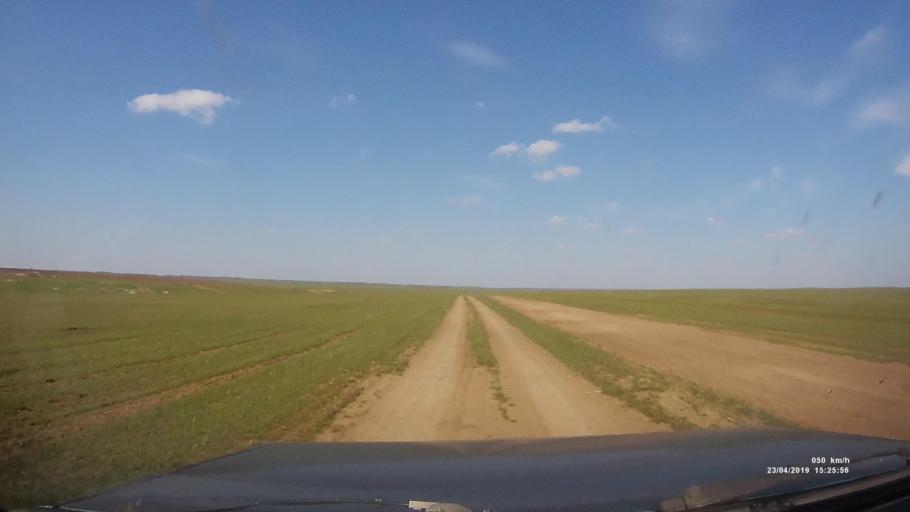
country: RU
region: Rostov
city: Remontnoye
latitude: 46.5435
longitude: 42.9855
